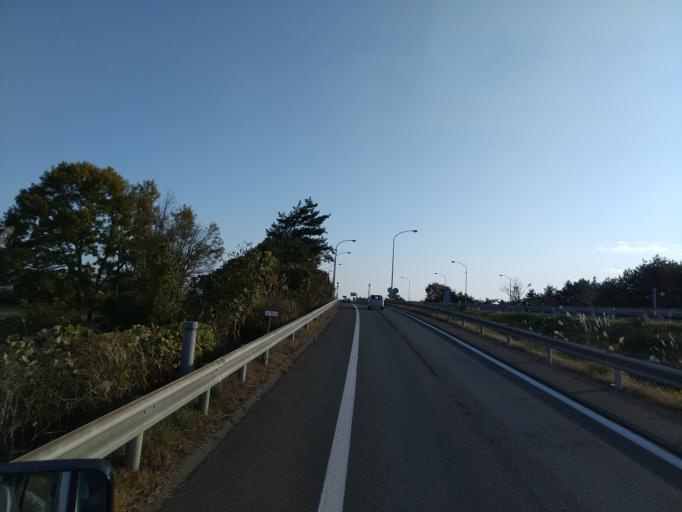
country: JP
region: Iwate
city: Morioka-shi
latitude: 39.6514
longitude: 141.1235
